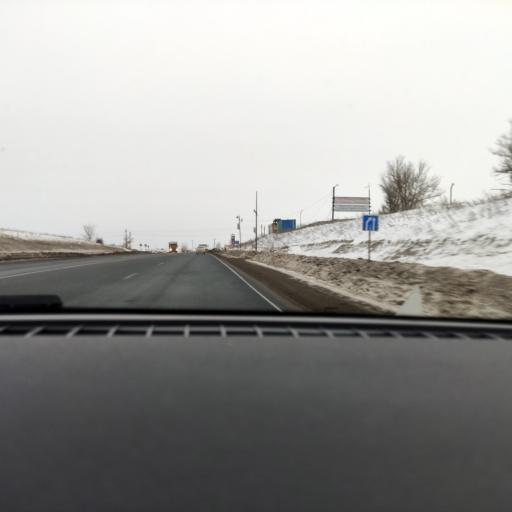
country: RU
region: Samara
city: Novosemeykino
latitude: 53.3932
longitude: 50.4271
